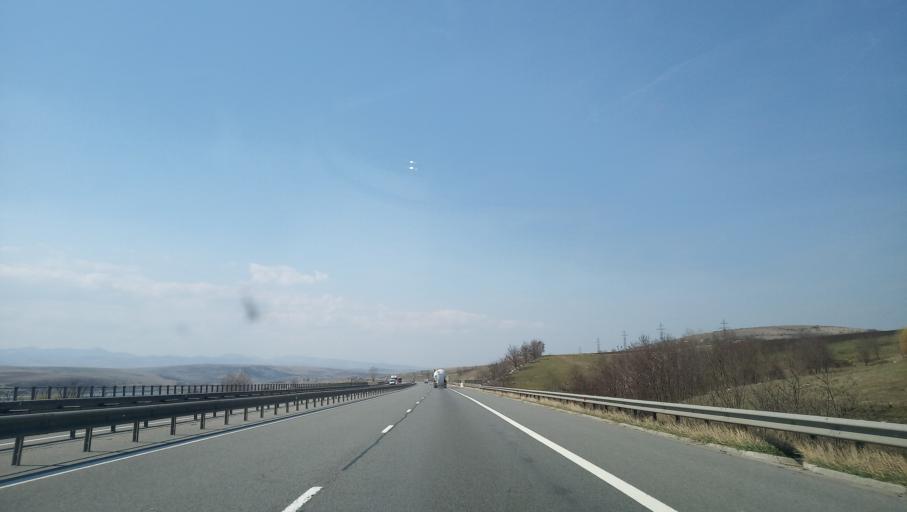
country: RO
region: Cluj
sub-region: Comuna Ciurila
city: Ciurila
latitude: 46.6246
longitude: 23.5722
